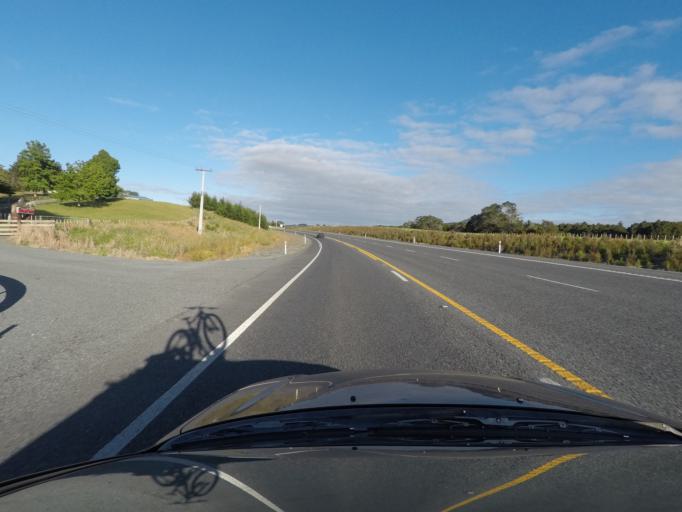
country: NZ
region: Northland
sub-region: Far North District
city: Kawakawa
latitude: -35.5008
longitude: 174.1747
